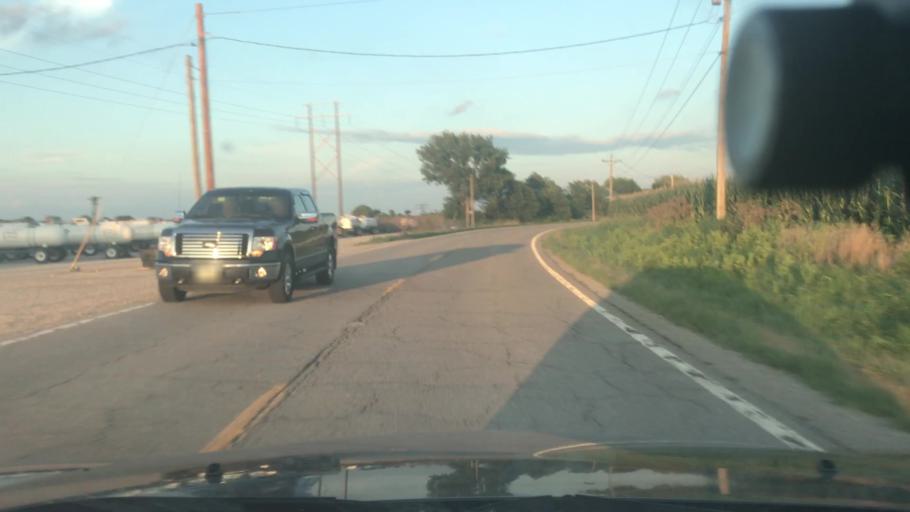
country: US
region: Illinois
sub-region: Washington County
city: Okawville
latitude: 38.4182
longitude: -89.5430
